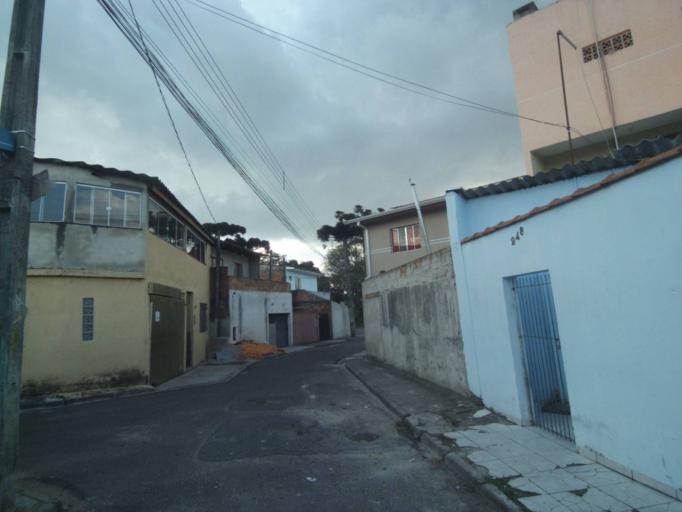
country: BR
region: Parana
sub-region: Sao Jose Dos Pinhais
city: Sao Jose dos Pinhais
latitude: -25.5344
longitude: -49.2793
